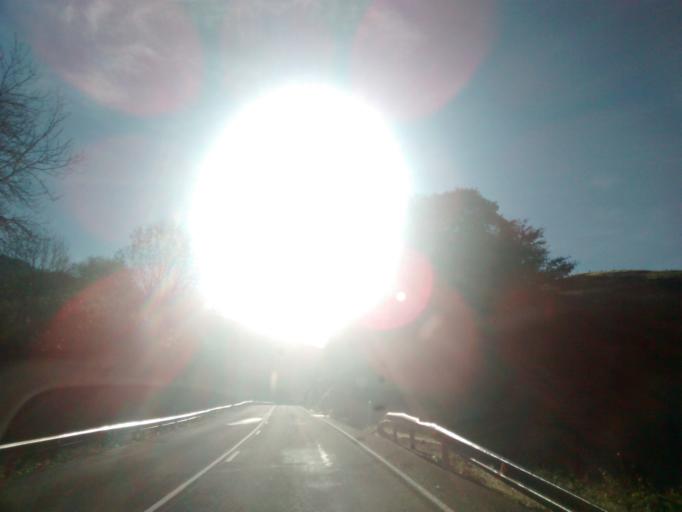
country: ES
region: Cantabria
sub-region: Provincia de Cantabria
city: Santiurde de Toranzo
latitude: 43.1601
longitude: -3.8967
